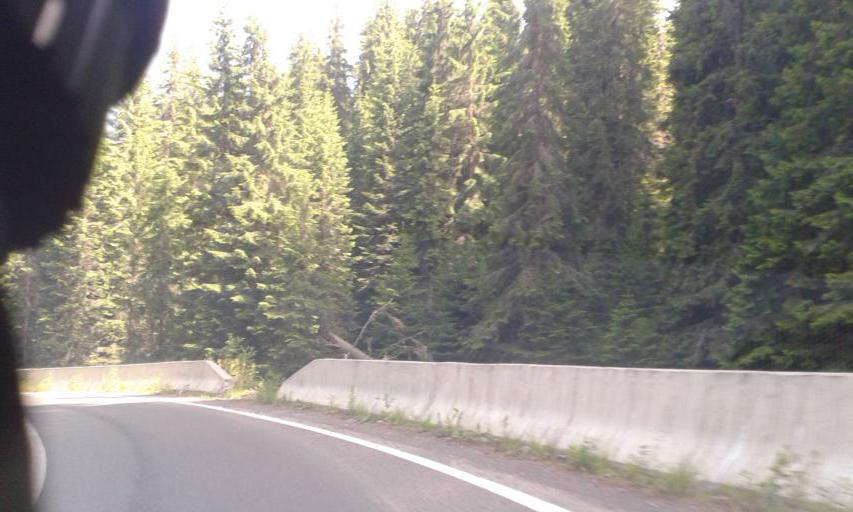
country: RO
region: Hunedoara
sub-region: Oras Petrila
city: Petrila
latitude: 45.5237
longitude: 23.6453
